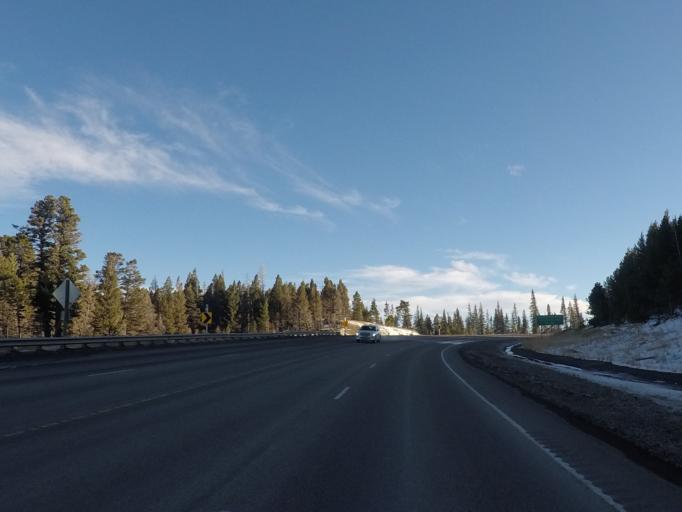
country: US
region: Montana
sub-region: Lewis and Clark County
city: Helena West Side
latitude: 46.5649
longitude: -112.3059
